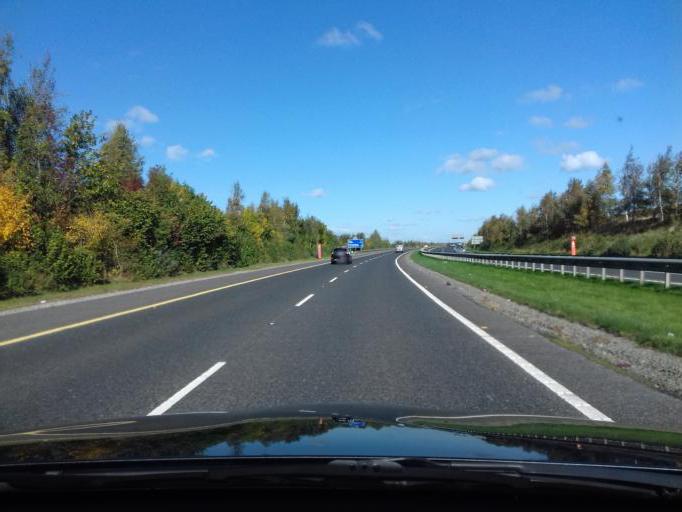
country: IE
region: Leinster
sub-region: Fingal County
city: Blanchardstown
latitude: 53.4432
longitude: -6.3558
